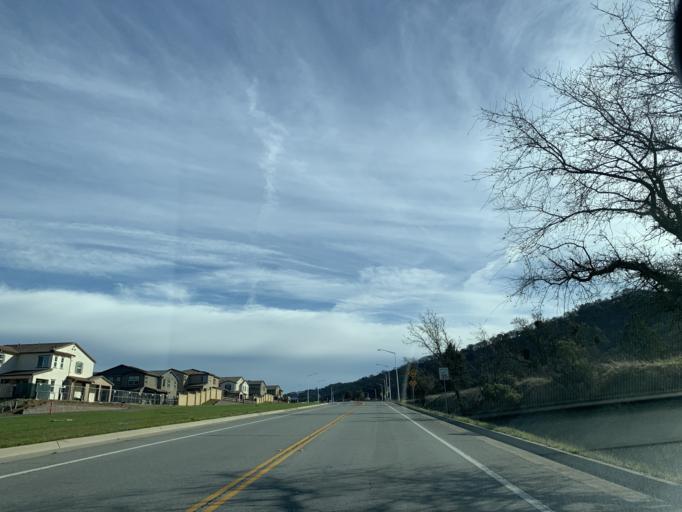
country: US
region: California
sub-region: Santa Clara County
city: Gilroy
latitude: 36.9958
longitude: -121.5958
